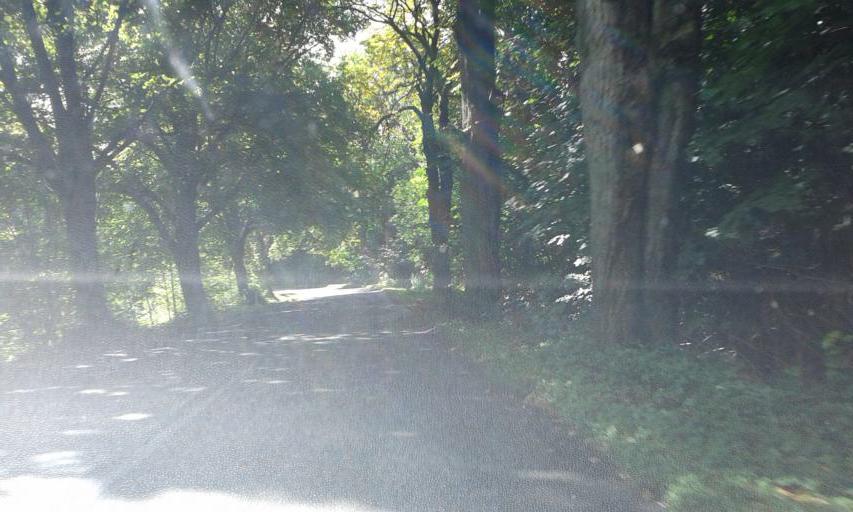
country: PL
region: West Pomeranian Voivodeship
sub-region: Powiat koszalinski
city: Bobolice
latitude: 53.9962
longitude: 16.7034
